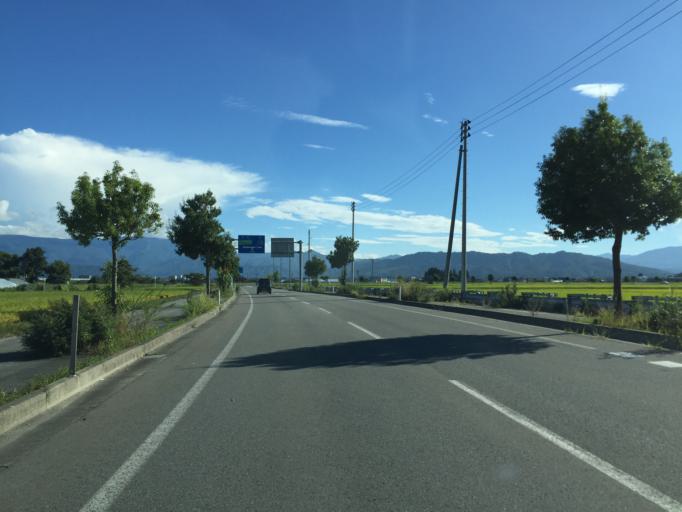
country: JP
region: Yamagata
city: Yonezawa
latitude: 37.9462
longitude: 140.1067
